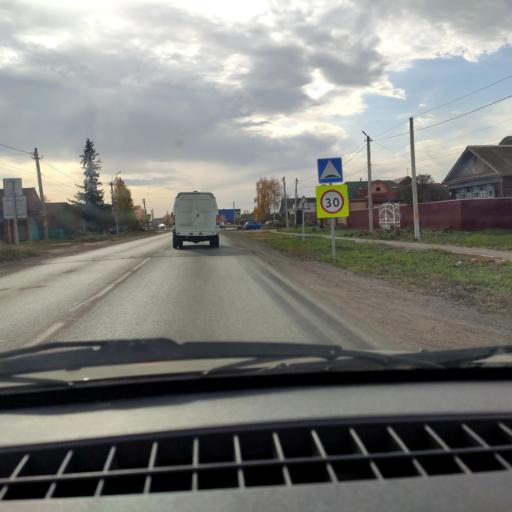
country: RU
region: Bashkortostan
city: Ufa
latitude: 54.6124
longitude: 55.9009
